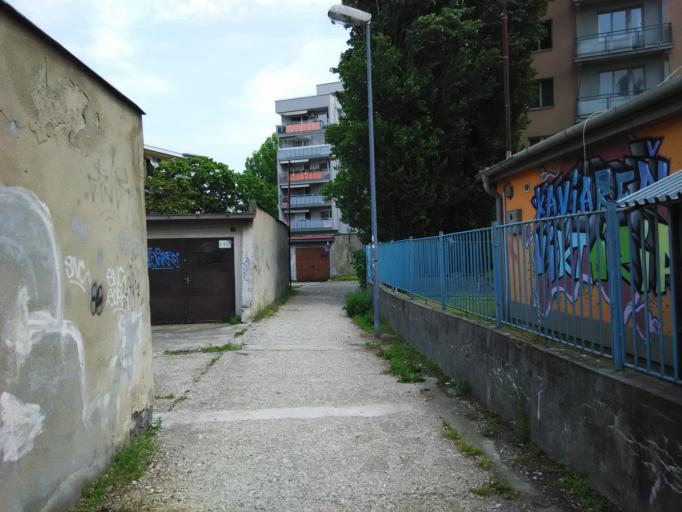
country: SK
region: Bratislavsky
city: Bratislava
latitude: 48.1632
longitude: 17.1496
